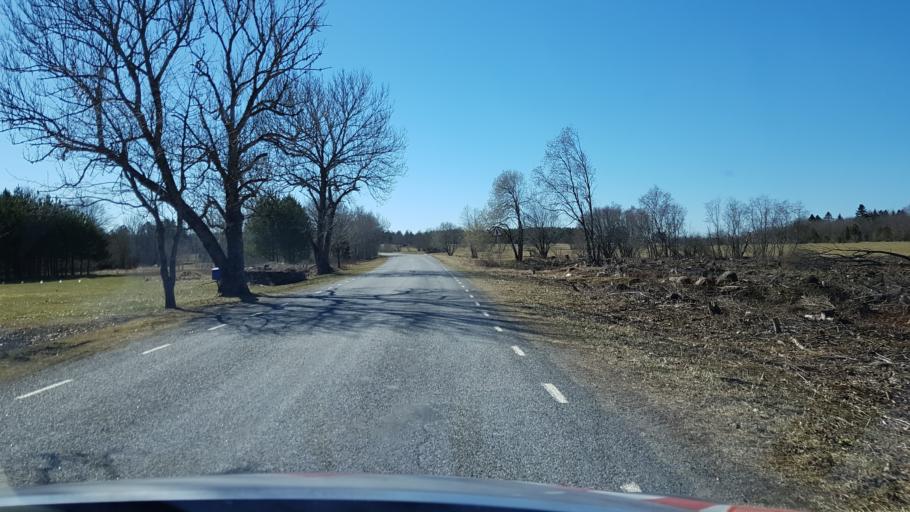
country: EE
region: Laeaene-Virumaa
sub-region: Haljala vald
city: Haljala
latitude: 59.5207
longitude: 26.2328
